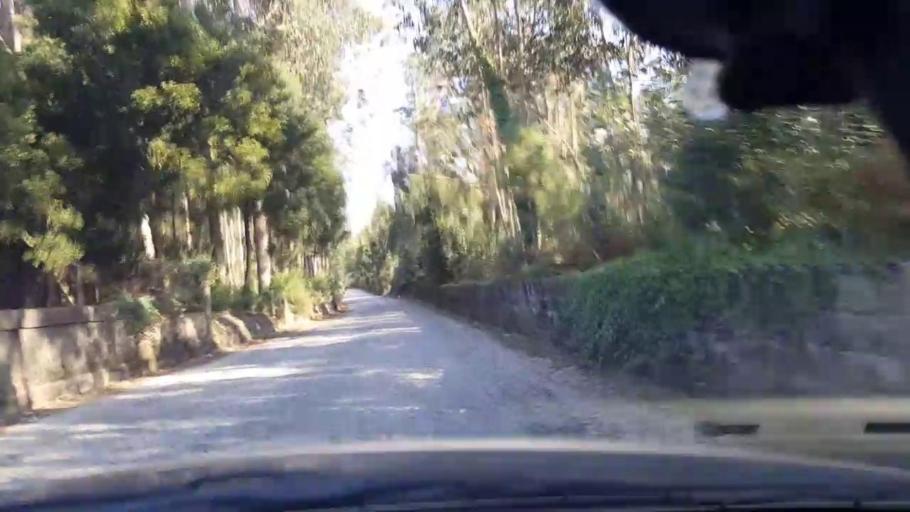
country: PT
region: Porto
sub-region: Vila do Conde
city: Arvore
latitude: 41.3526
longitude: -8.7041
